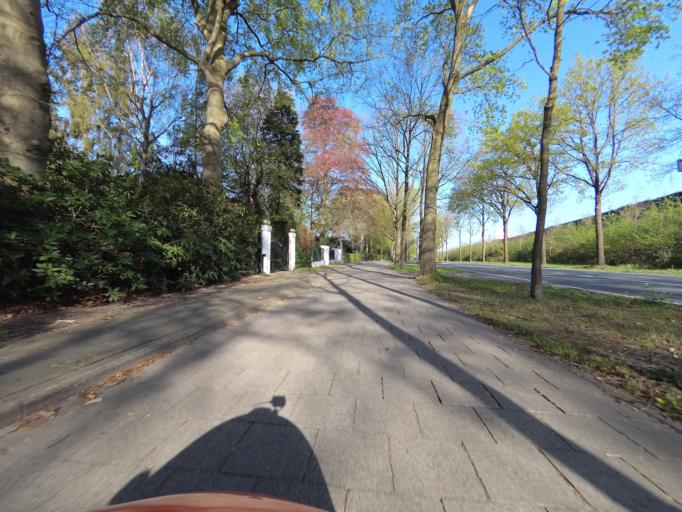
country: NL
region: North Holland
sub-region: Gemeente Laren
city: Laren
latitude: 52.2684
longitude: 5.2005
